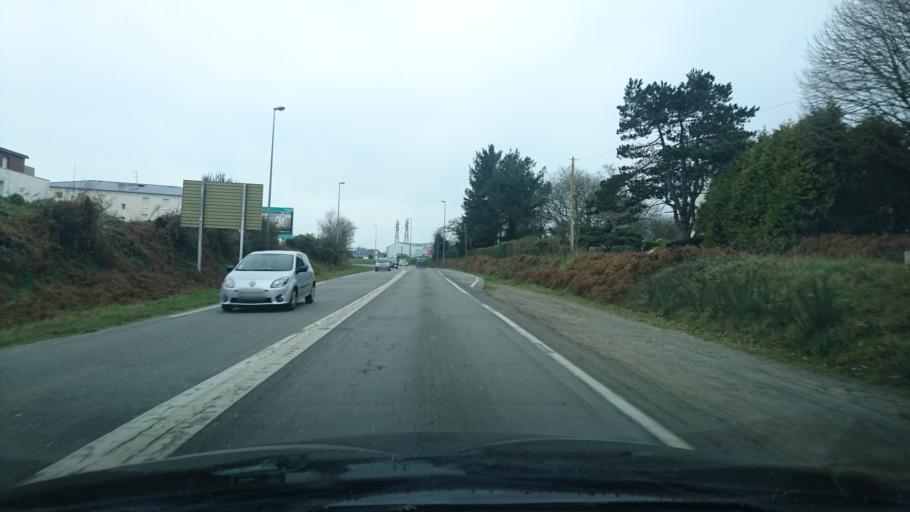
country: FR
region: Brittany
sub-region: Departement du Finistere
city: Guilers
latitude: 48.3943
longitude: -4.5390
